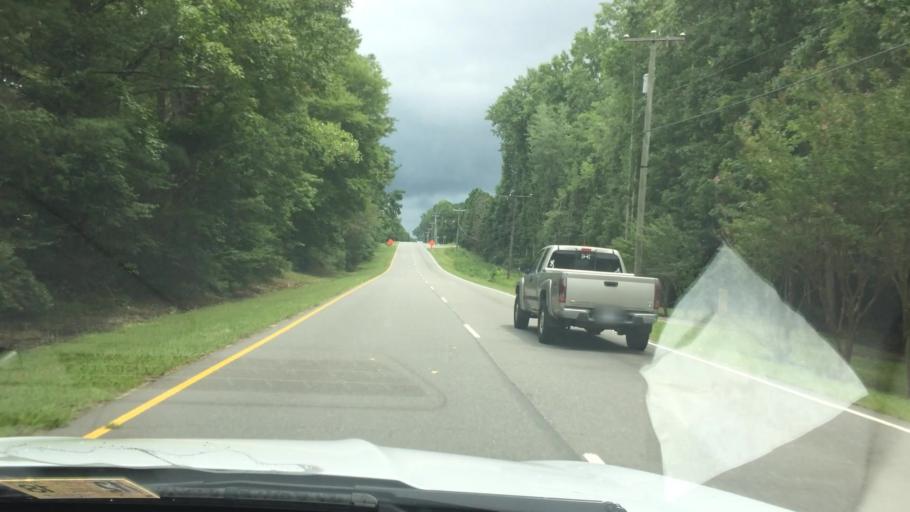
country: US
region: Virginia
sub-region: King William County
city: West Point
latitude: 37.4035
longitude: -76.8298
